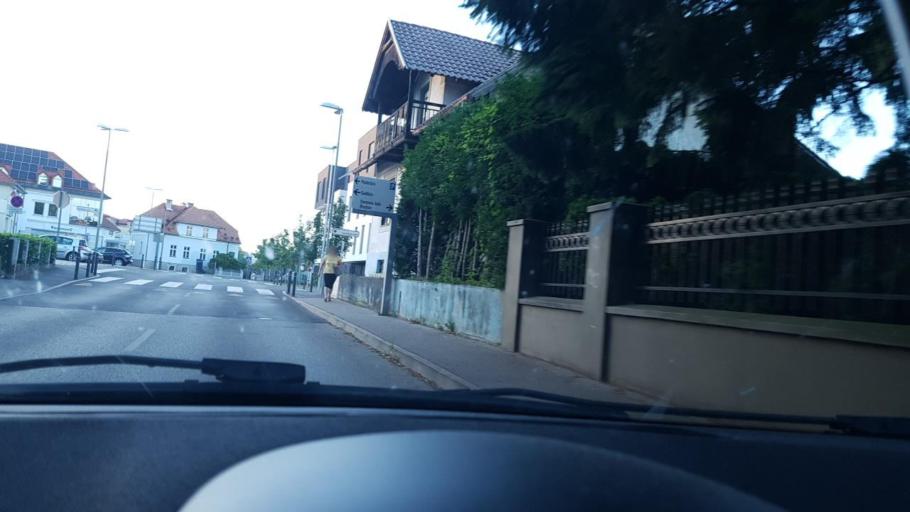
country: SI
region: Brezice
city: Brezice
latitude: 45.9064
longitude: 15.5936
